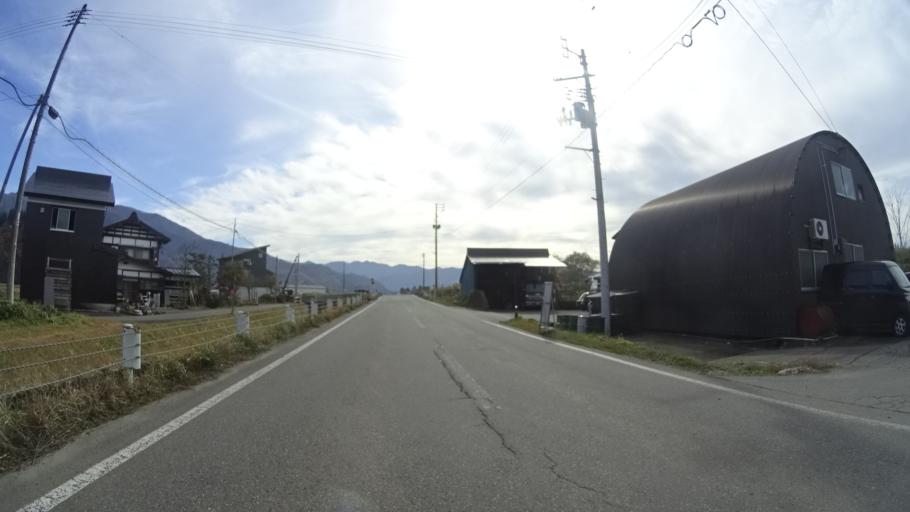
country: JP
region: Niigata
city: Muikamachi
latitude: 37.0497
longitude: 138.8807
